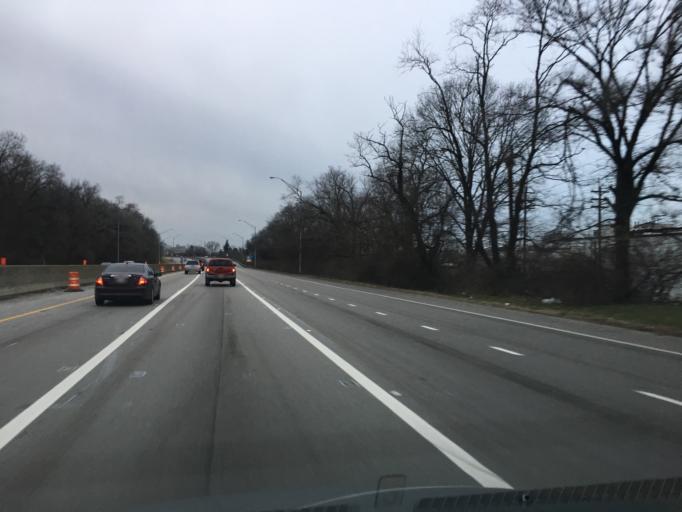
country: US
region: Ohio
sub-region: Hamilton County
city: Elmwood Place
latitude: 39.1929
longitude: -84.4776
